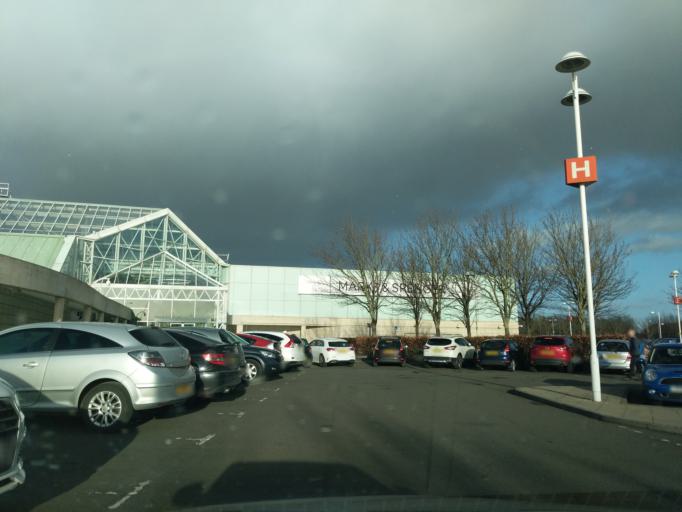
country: GB
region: Scotland
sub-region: Edinburgh
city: Currie
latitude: 55.9378
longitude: -3.3130
